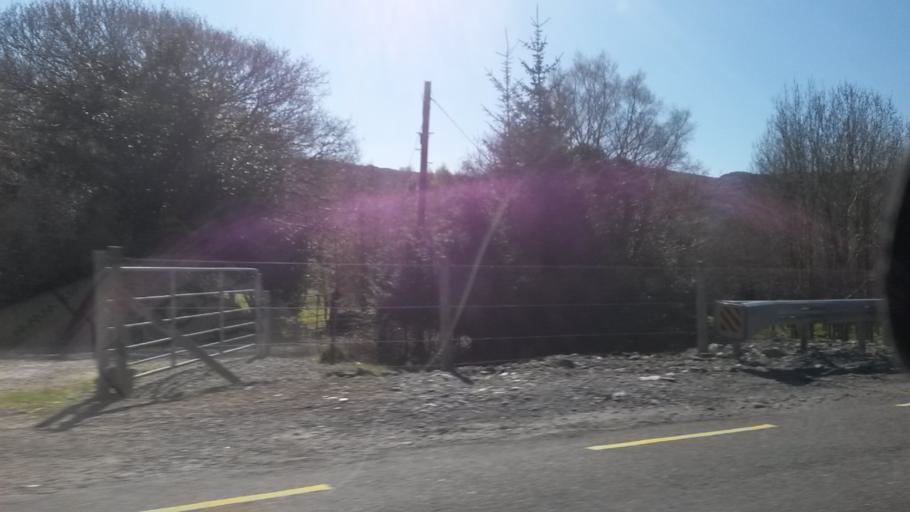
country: IE
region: Munster
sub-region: Ciarrai
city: Cill Airne
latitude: 51.9687
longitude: -9.3502
